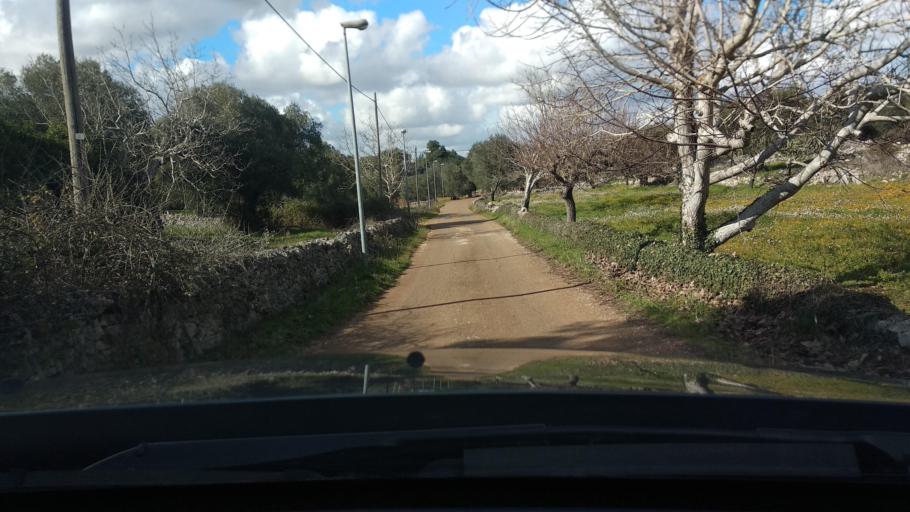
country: IT
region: Apulia
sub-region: Provincia di Brindisi
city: Casalini
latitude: 40.6945
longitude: 17.4853
